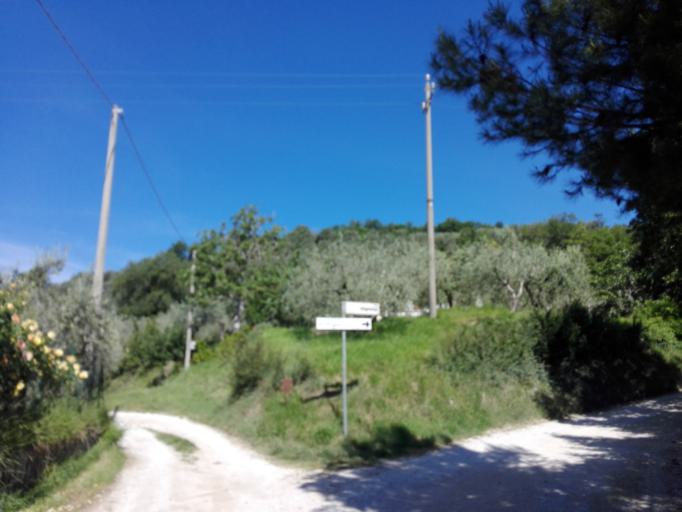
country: IT
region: Umbria
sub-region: Provincia di Perugia
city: Foligno
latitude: 42.9682
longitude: 12.7427
